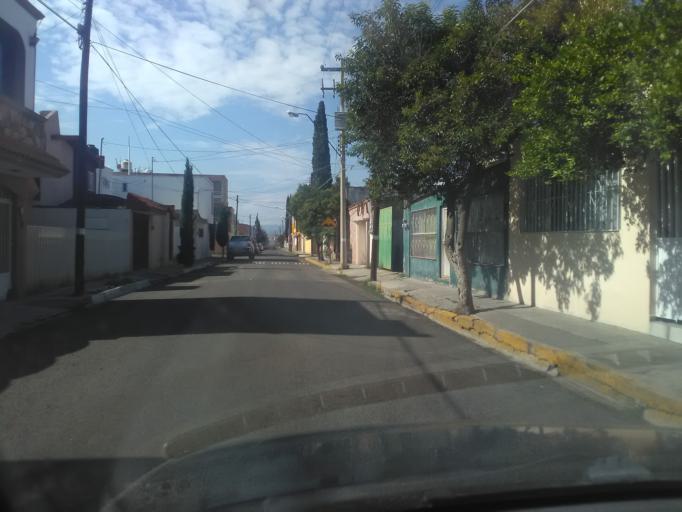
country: MX
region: Durango
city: Victoria de Durango
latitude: 24.0232
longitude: -104.6579
